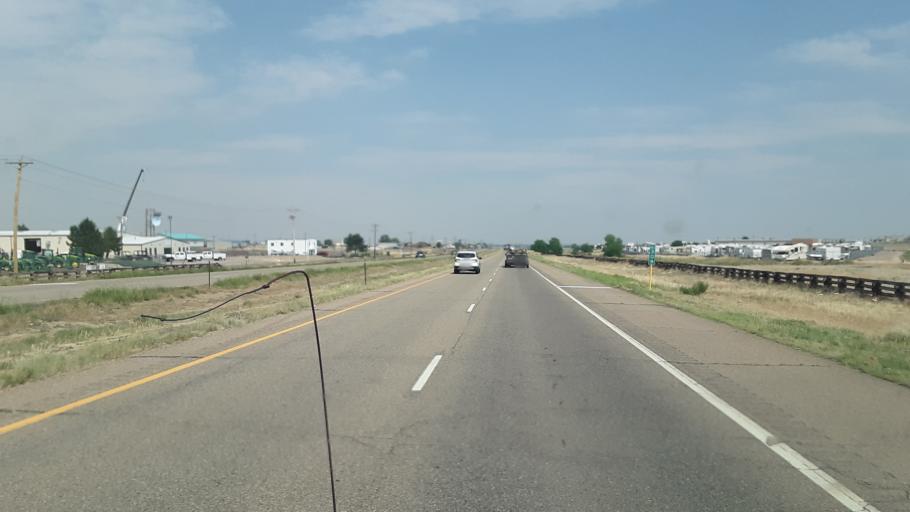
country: US
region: Colorado
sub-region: Pueblo County
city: Pueblo West
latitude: 38.3277
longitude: -104.7155
